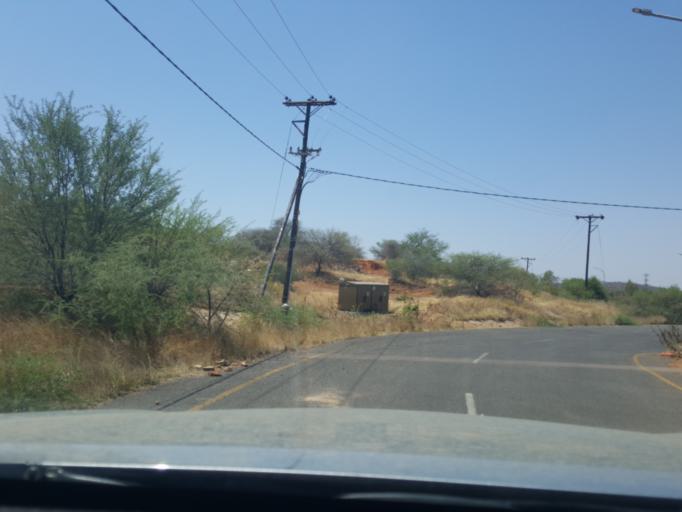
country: BW
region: South East
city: Lobatse
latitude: -25.1861
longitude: 25.6791
